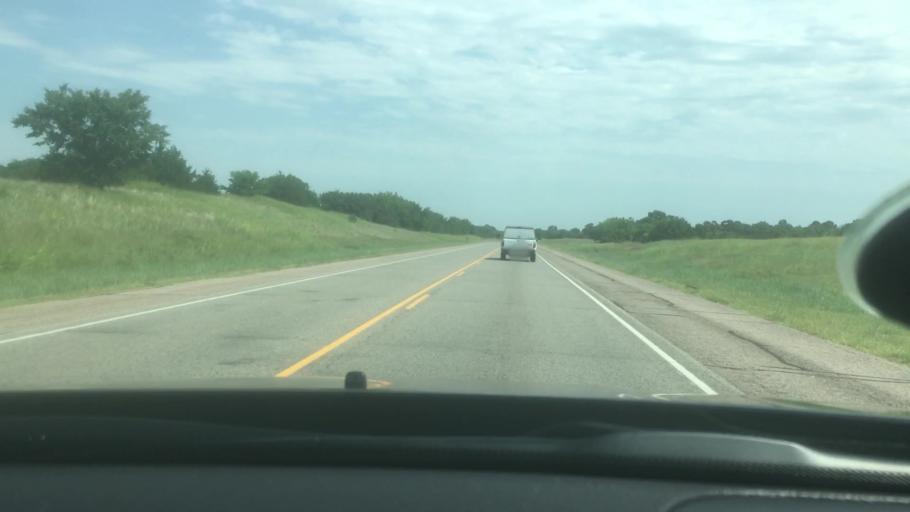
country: US
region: Oklahoma
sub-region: Seminole County
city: Maud
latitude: 35.0316
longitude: -96.9314
